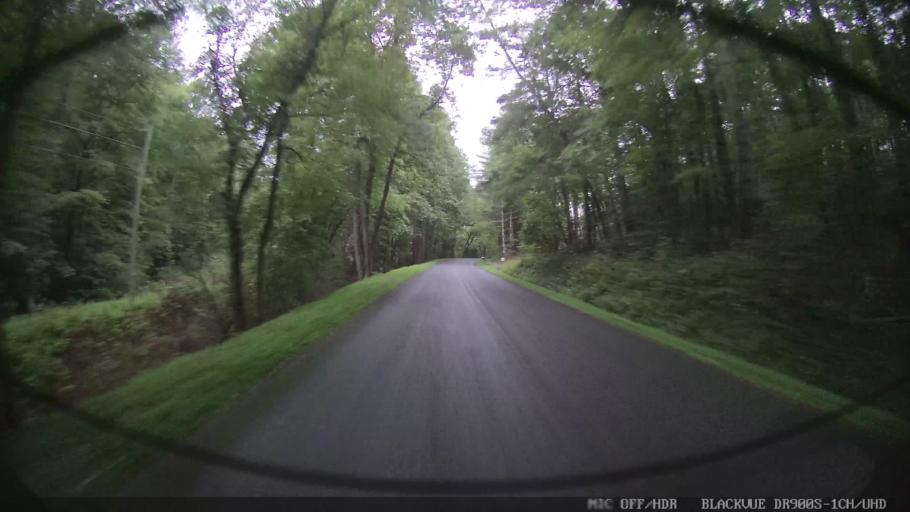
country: US
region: Georgia
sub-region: Gilmer County
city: Ellijay
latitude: 34.7779
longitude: -84.5420
